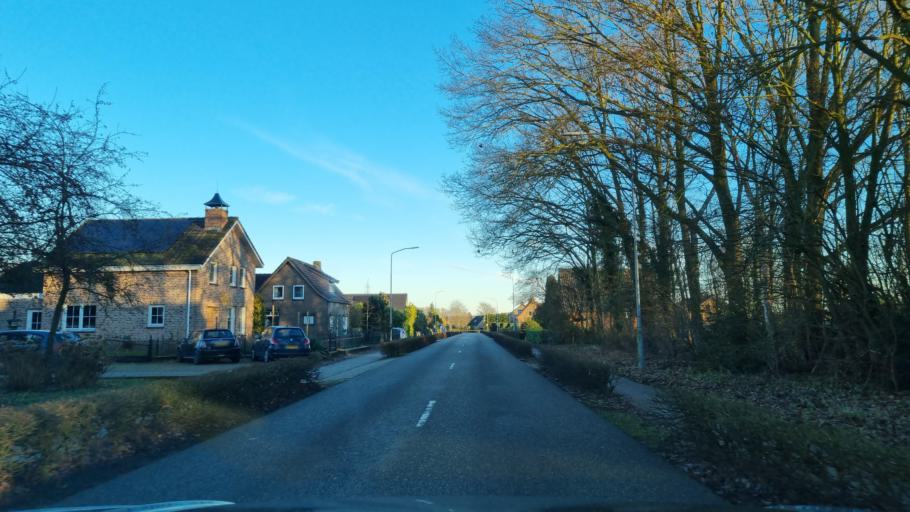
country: NL
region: Gelderland
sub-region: Gemeente Groesbeek
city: De Horst
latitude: 51.7727
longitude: 5.9546
